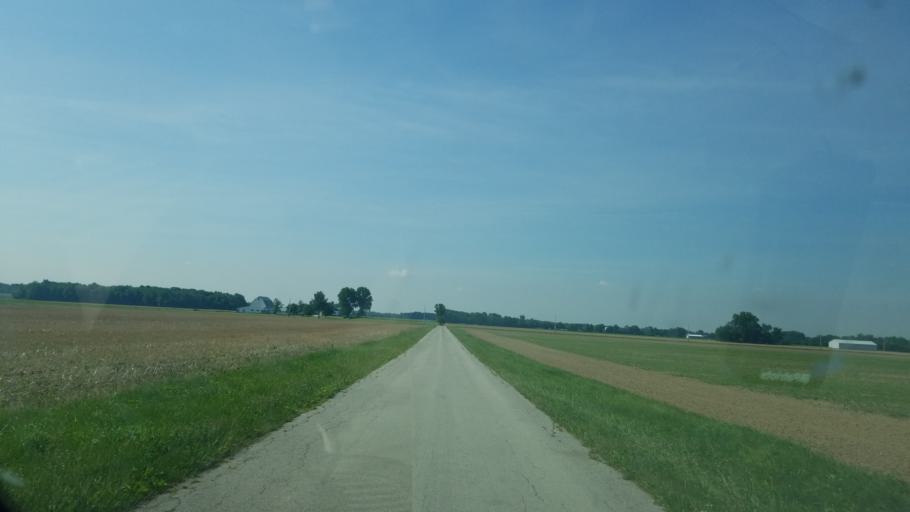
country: US
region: Ohio
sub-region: Wyandot County
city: Carey
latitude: 40.9816
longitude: -83.3193
